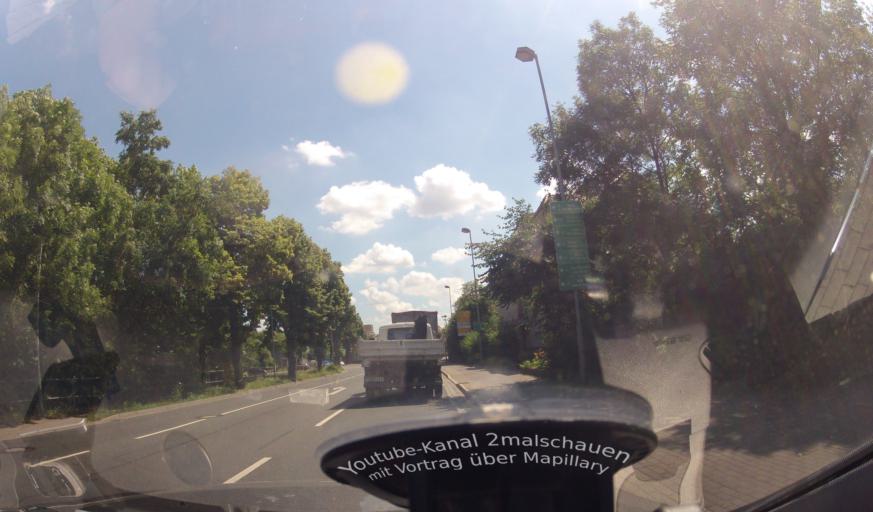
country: DE
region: Saxony
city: Torgau
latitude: 51.5577
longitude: 12.9929
